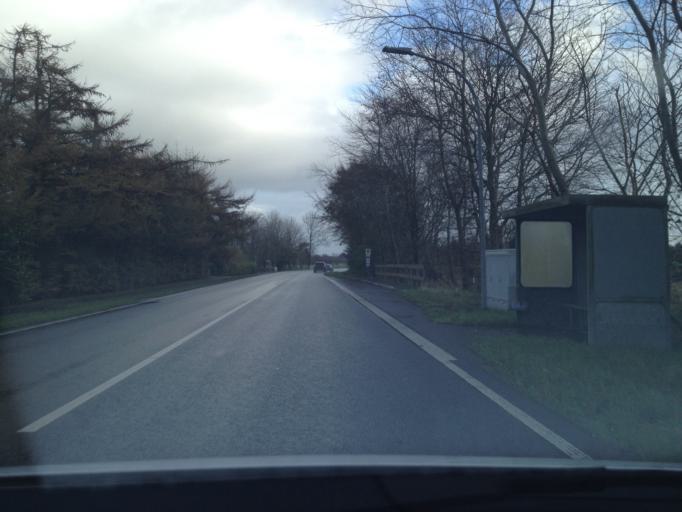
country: DE
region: Schleswig-Holstein
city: Klixbull
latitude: 54.7933
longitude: 8.9145
